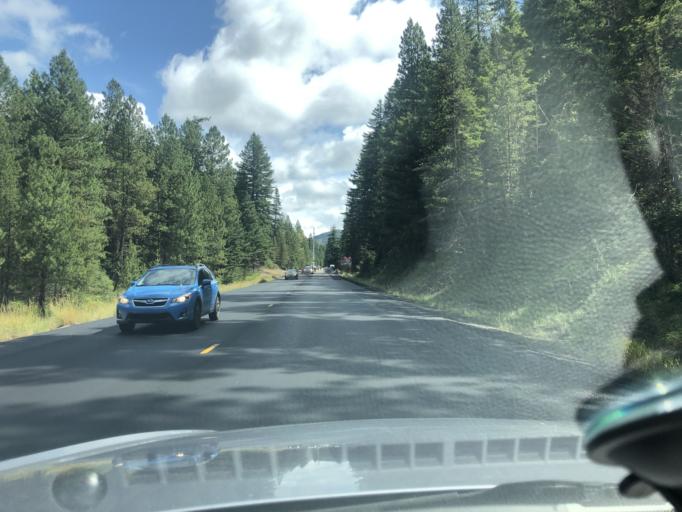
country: US
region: Washington
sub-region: Chelan County
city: Leavenworth
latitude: 47.3264
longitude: -120.6692
